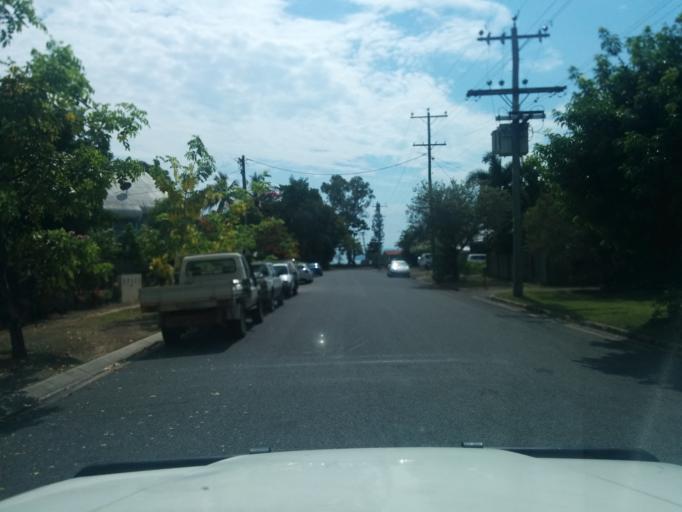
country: AU
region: Queensland
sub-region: Cairns
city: Yorkeys Knob
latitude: -16.8425
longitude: 145.7411
